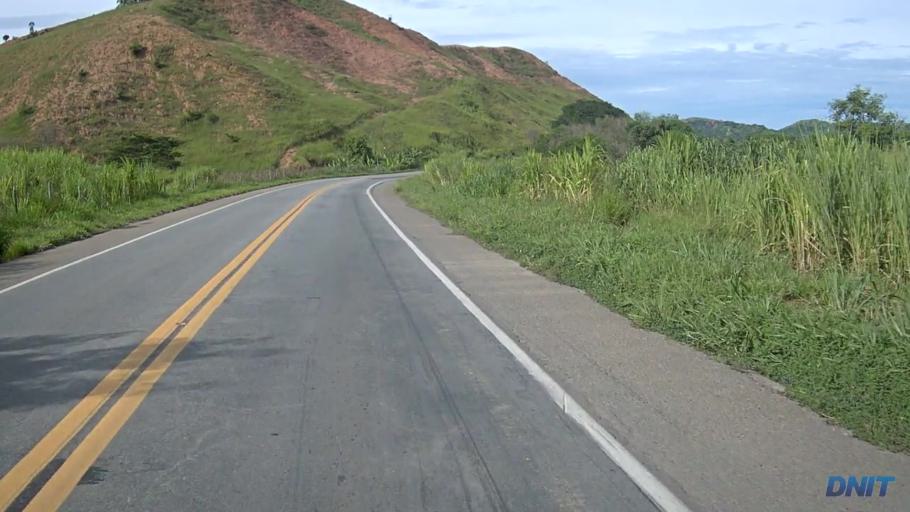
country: BR
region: Minas Gerais
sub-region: Belo Oriente
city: Belo Oriente
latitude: -19.1746
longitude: -42.2540
